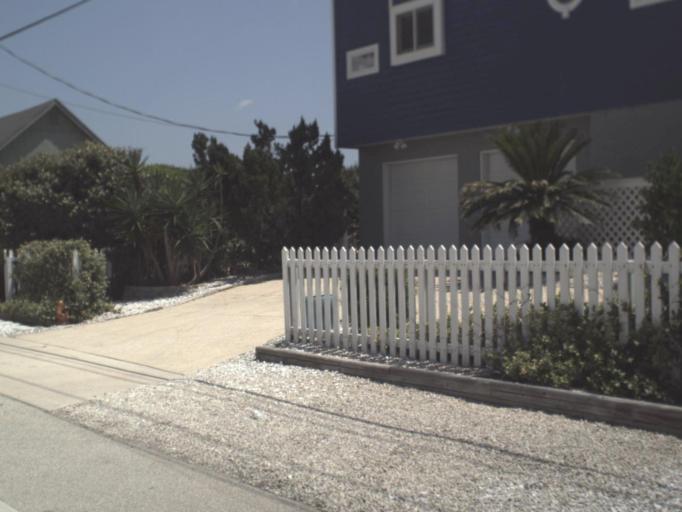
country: US
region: Florida
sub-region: Saint Johns County
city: Villano Beach
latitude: 30.0093
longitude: -81.3199
